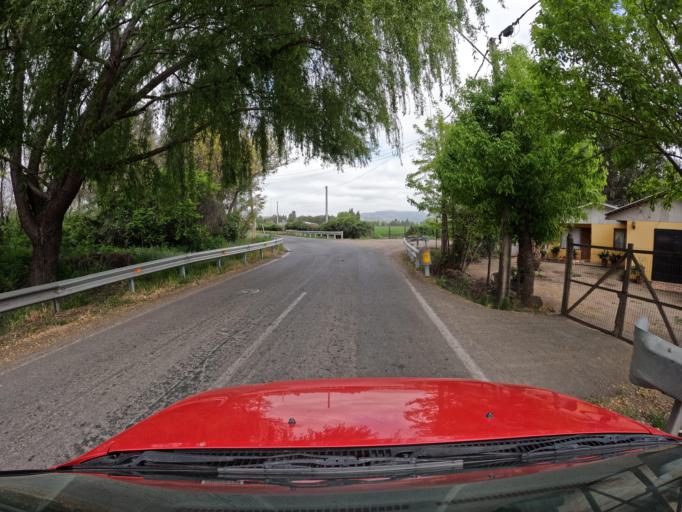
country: CL
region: O'Higgins
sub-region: Provincia de Colchagua
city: Santa Cruz
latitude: -34.6734
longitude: -71.3495
